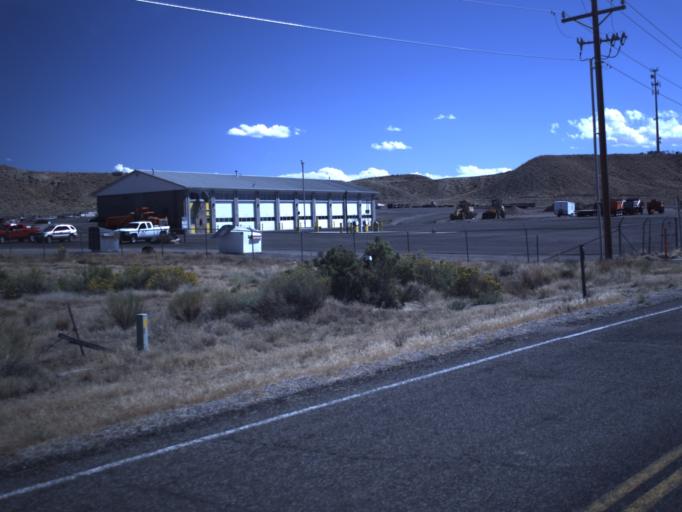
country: US
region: Utah
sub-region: Grand County
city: Moab
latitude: 38.9673
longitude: -109.7155
